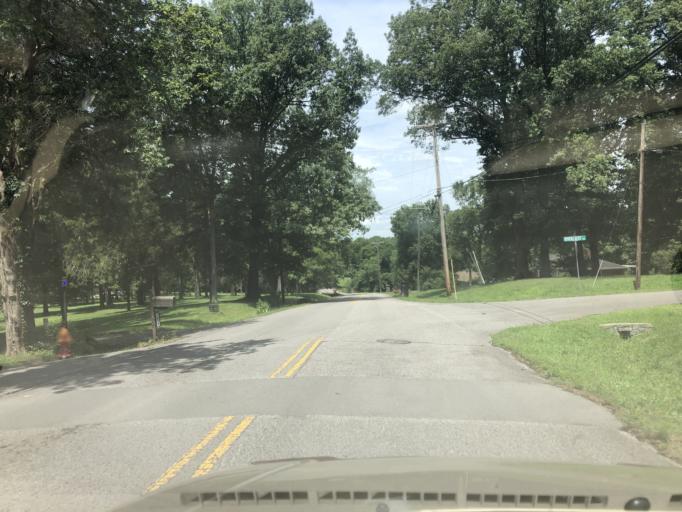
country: US
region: Tennessee
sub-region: Davidson County
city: Lakewood
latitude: 36.2458
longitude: -86.6862
